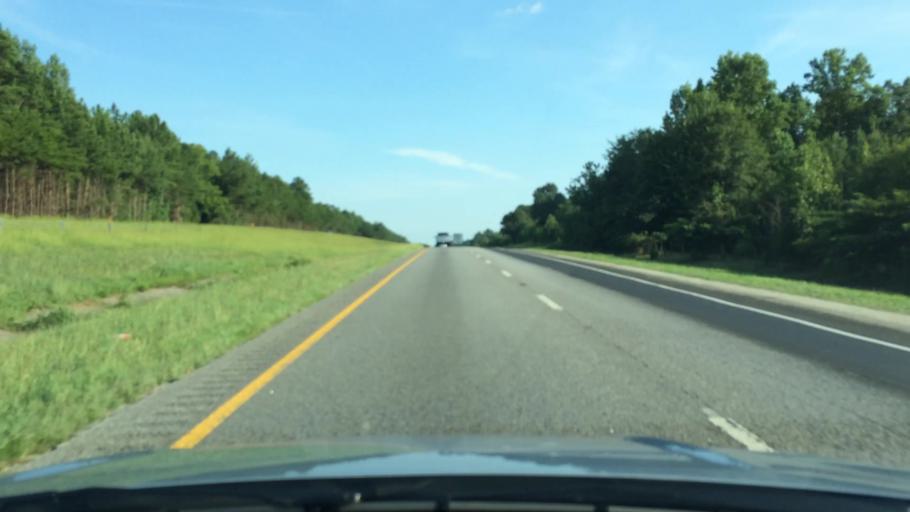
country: US
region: South Carolina
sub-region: Spartanburg County
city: Roebuck
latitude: 34.8156
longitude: -81.9629
